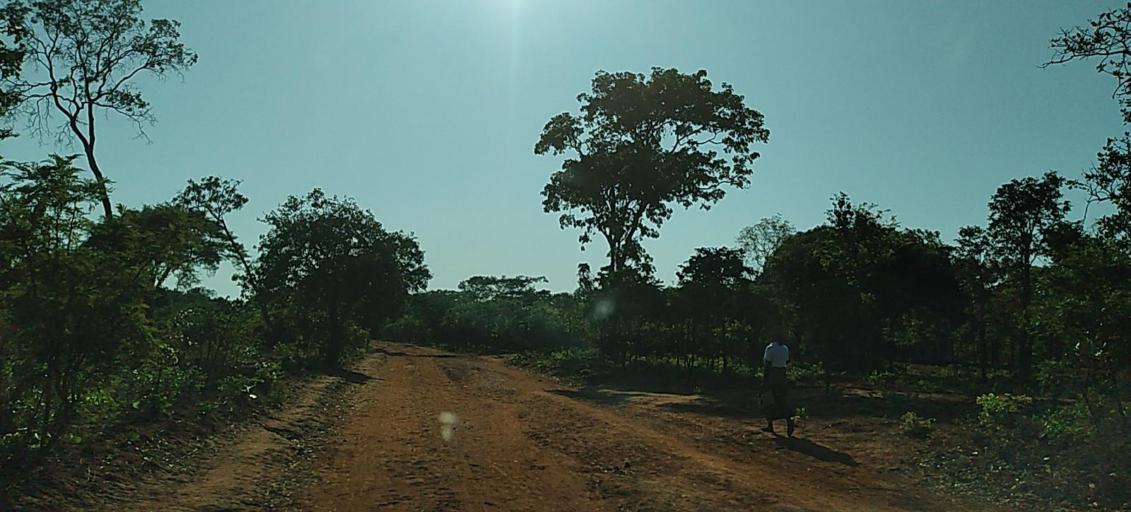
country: ZM
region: Copperbelt
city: Luanshya
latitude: -13.4592
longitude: 28.8141
